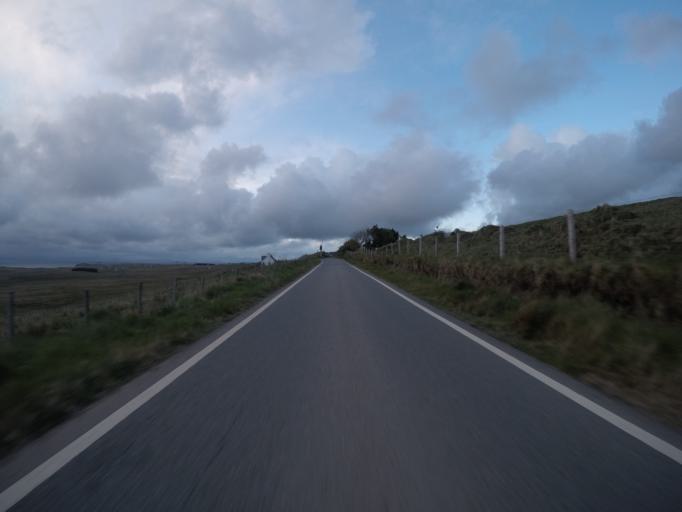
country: GB
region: Scotland
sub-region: Highland
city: Portree
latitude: 57.6317
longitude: -6.3778
